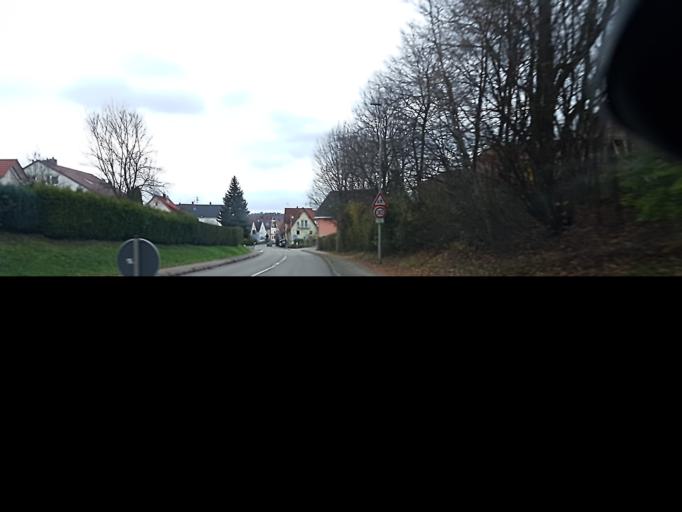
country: DE
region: Baden-Wuerttemberg
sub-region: Regierungsbezirk Stuttgart
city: Aspach
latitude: 48.9922
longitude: 9.3587
